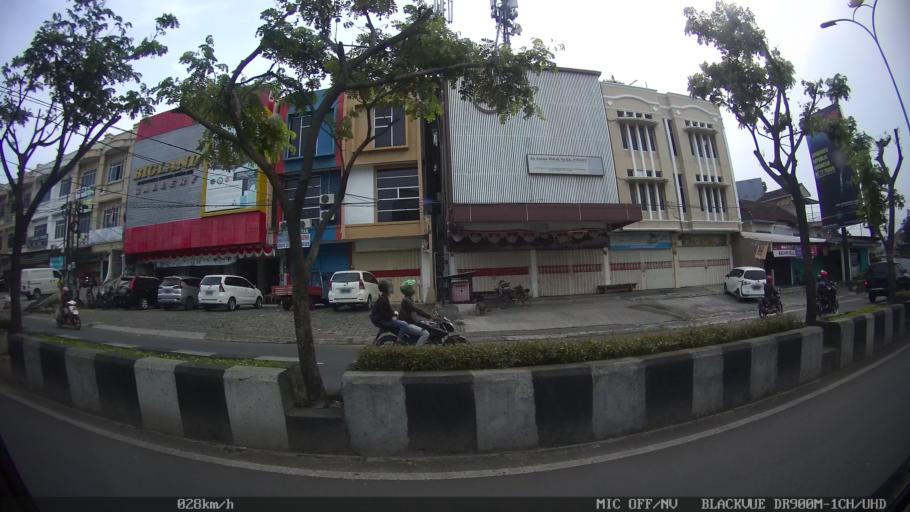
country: ID
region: Lampung
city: Bandarlampung
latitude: -5.4184
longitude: 105.2687
